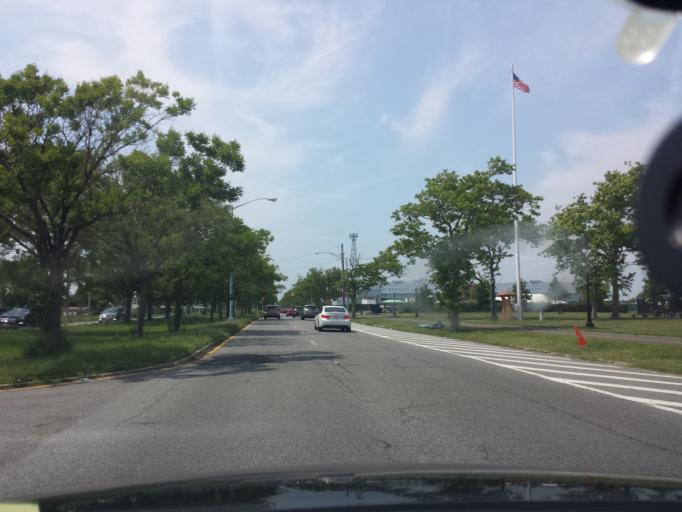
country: US
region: New York
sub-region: Kings County
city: East New York
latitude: 40.5872
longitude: -73.8975
